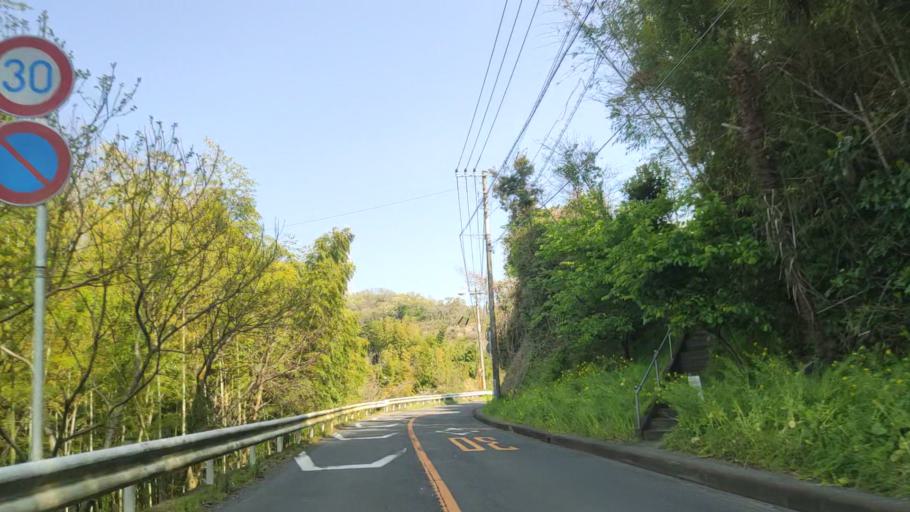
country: JP
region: Kanagawa
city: Ninomiya
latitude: 35.3168
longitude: 139.2729
